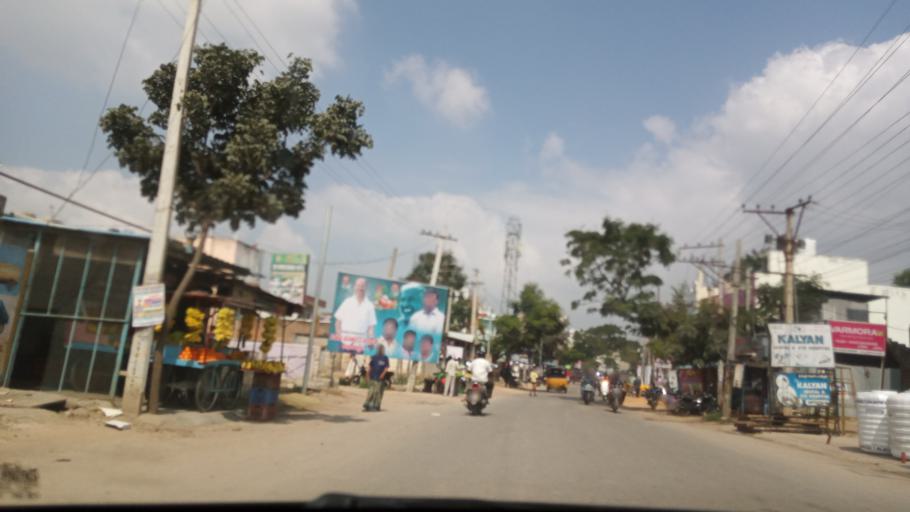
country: IN
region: Andhra Pradesh
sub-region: Chittoor
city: Madanapalle
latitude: 13.5593
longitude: 78.5096
